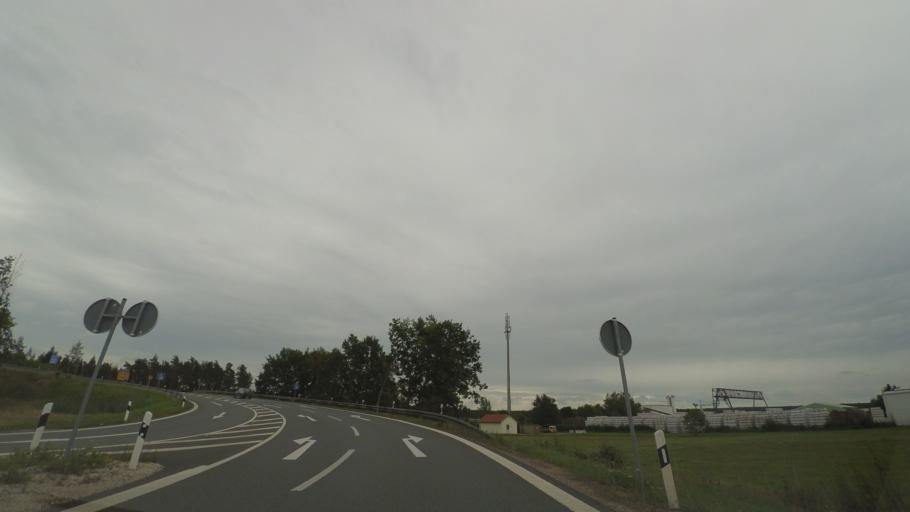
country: DE
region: Bavaria
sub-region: Upper Palatinate
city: Ebermannsdorf
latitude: 49.3998
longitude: 11.9792
